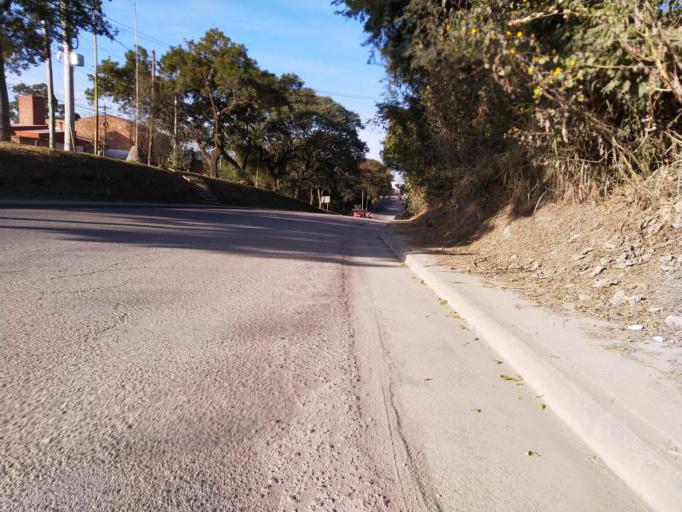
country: AR
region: Jujuy
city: San Salvador de Jujuy
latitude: -24.1797
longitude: -65.3412
